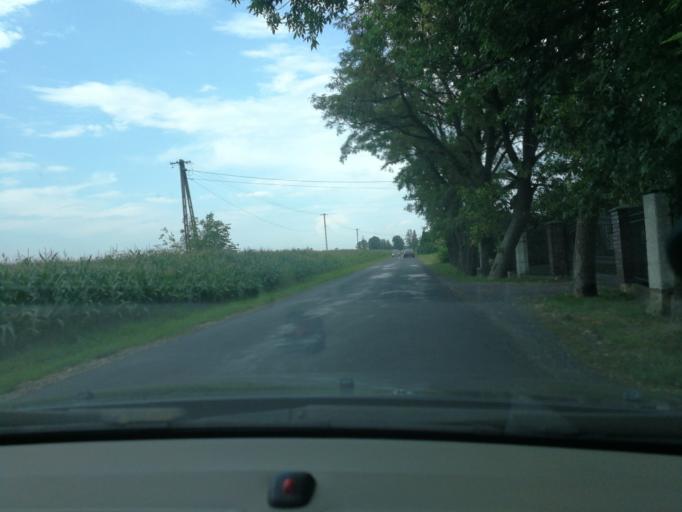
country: PL
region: Masovian Voivodeship
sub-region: Powiat grodziski
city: Grodzisk Mazowiecki
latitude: 52.1275
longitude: 20.5849
